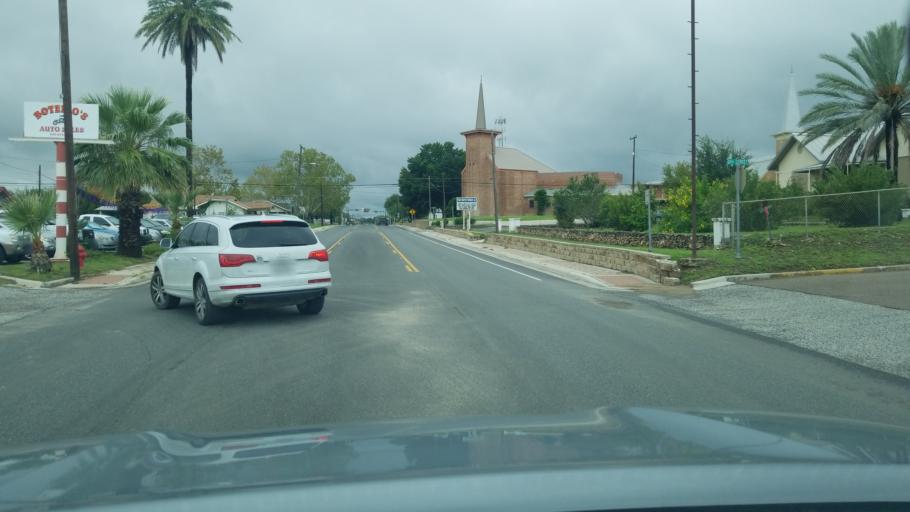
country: US
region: Texas
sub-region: Dimmit County
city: Carrizo Springs
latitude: 28.5221
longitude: -99.8612
